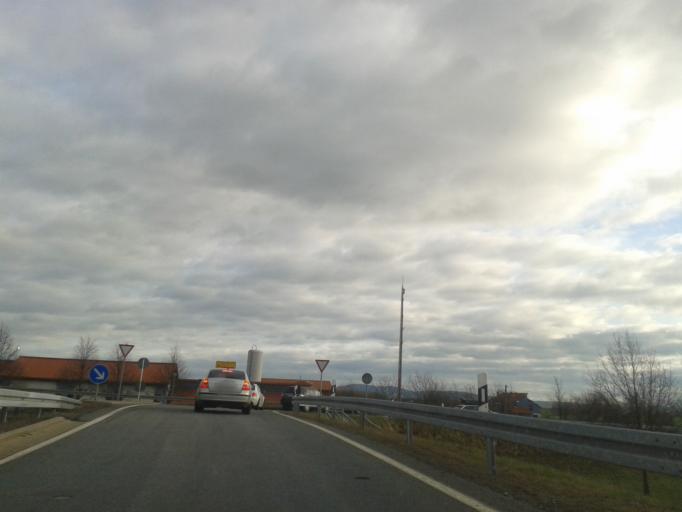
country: DE
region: Saxony
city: Weissenberg
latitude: 51.2051
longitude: 14.6632
